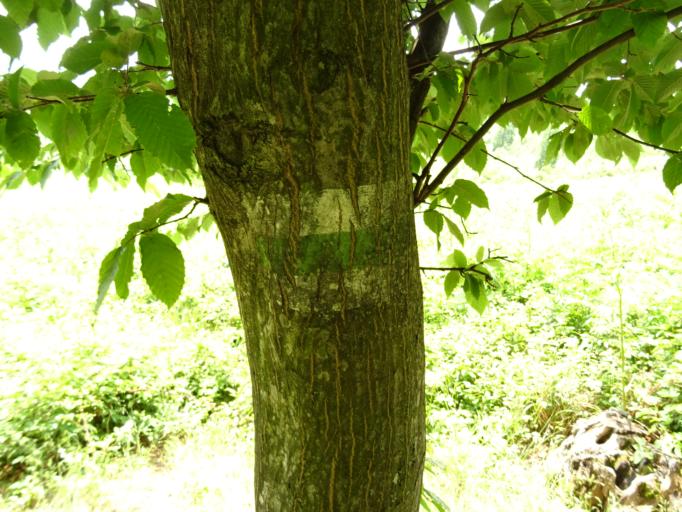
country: HU
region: Borsod-Abauj-Zemplen
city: Szendro
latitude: 48.5304
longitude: 20.8140
